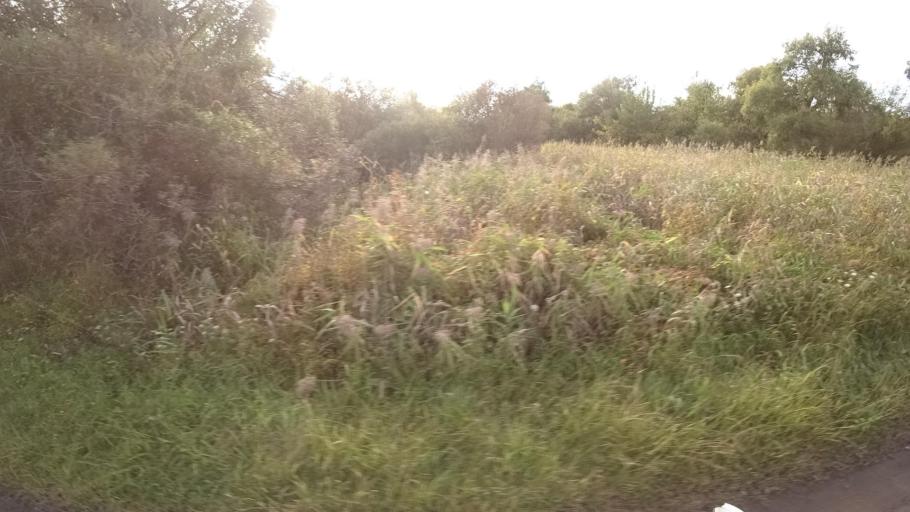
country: RU
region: Primorskiy
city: Dostoyevka
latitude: 44.2926
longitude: 133.4300
